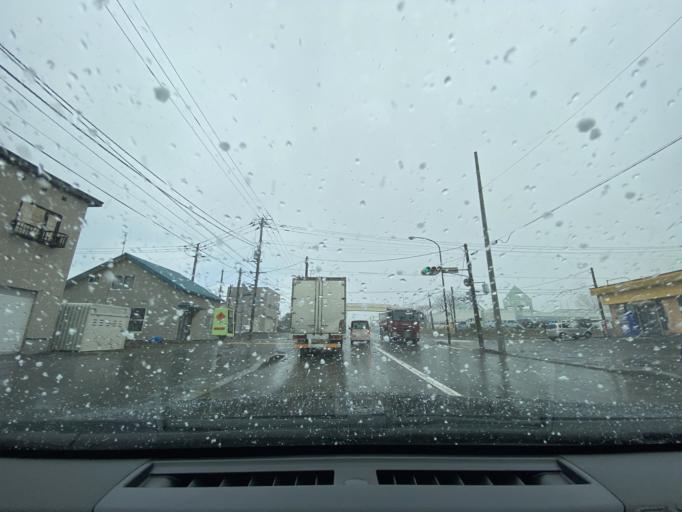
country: JP
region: Hokkaido
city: Takikawa
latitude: 43.6293
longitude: 141.9430
